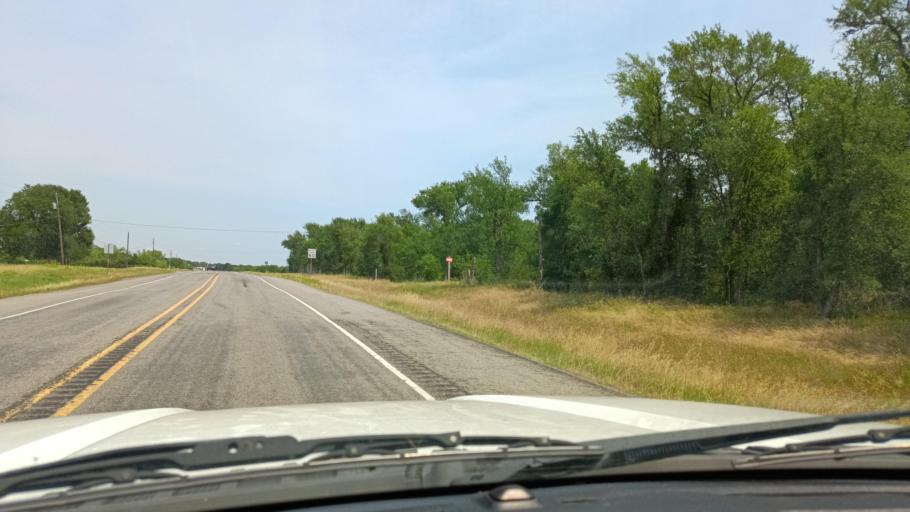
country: US
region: Texas
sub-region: Bell County
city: Rogers
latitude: 30.8770
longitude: -97.1392
